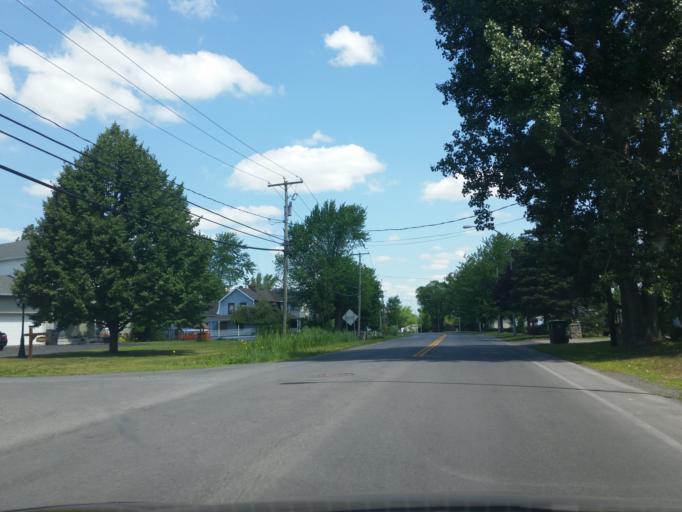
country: CA
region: Quebec
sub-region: Monteregie
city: Saint-Jean-sur-Richelieu
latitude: 45.3604
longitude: -73.2681
